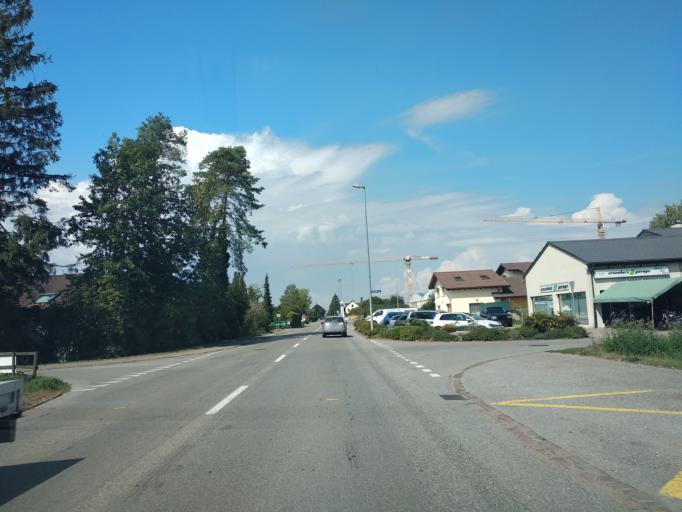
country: CH
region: Thurgau
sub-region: Frauenfeld District
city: Gachnang
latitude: 47.5666
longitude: 8.8588
